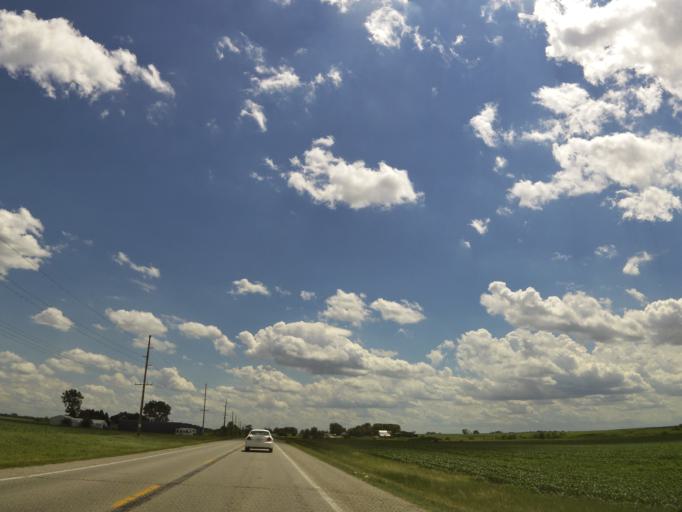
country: US
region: Iowa
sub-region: Buchanan County
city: Independence
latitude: 42.4167
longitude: -91.8899
